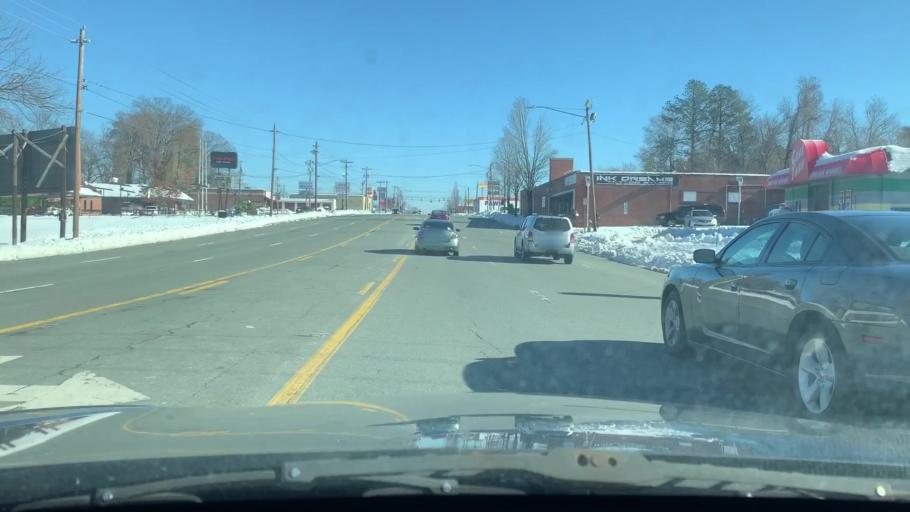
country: US
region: North Carolina
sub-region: Alamance County
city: Burlington
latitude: 36.0977
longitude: -79.4173
